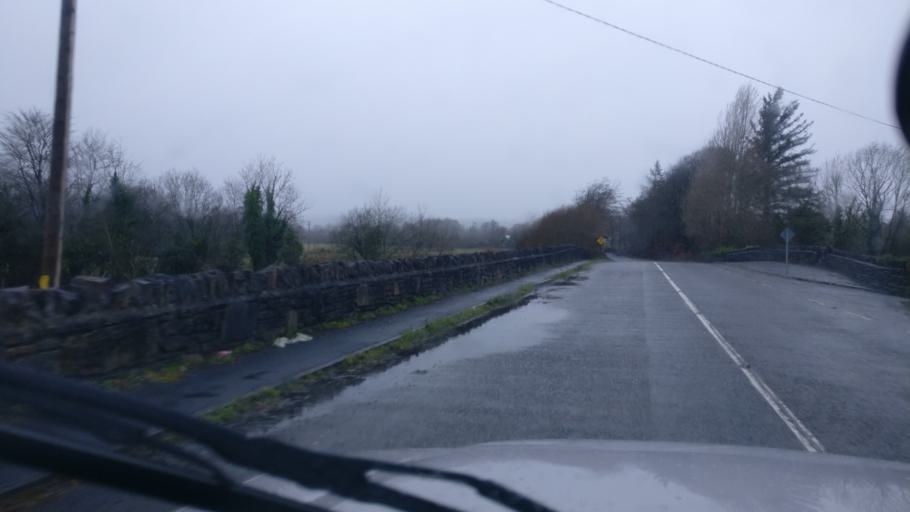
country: IE
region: Connaught
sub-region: County Galway
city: Loughrea
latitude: 53.1291
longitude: -8.4517
